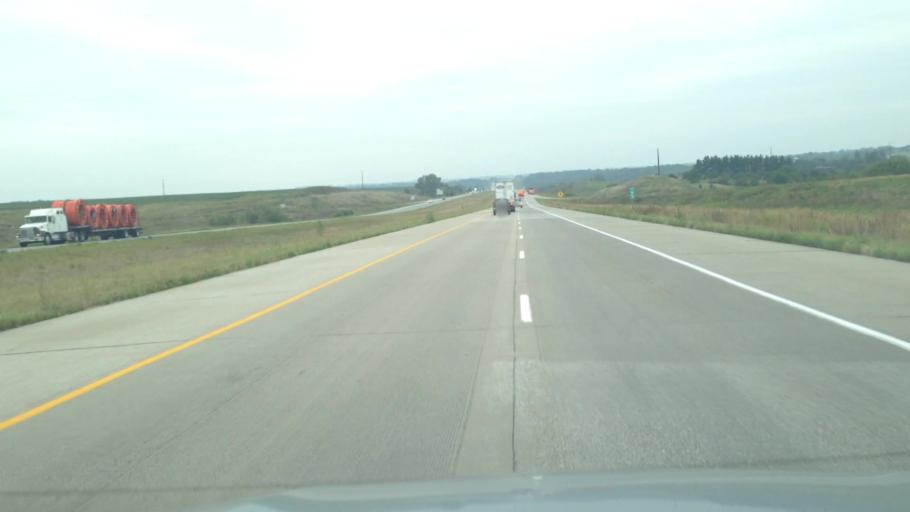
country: US
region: Iowa
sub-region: Warren County
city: Norwalk
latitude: 41.4826
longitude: -93.7805
